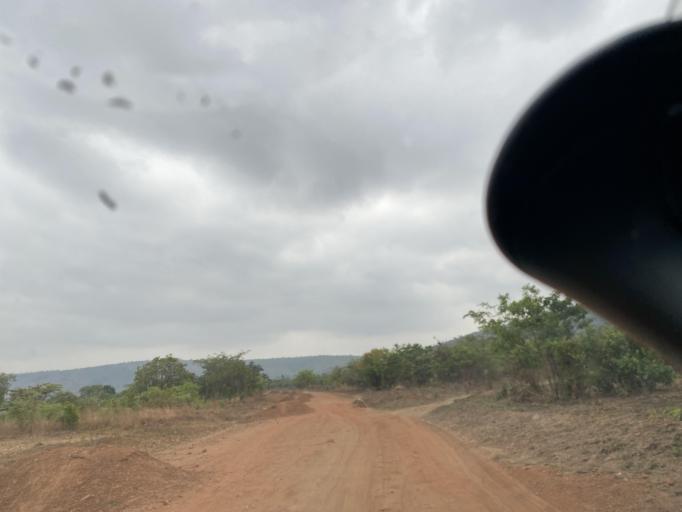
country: ZM
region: Lusaka
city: Chongwe
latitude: -15.1948
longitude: 28.7658
